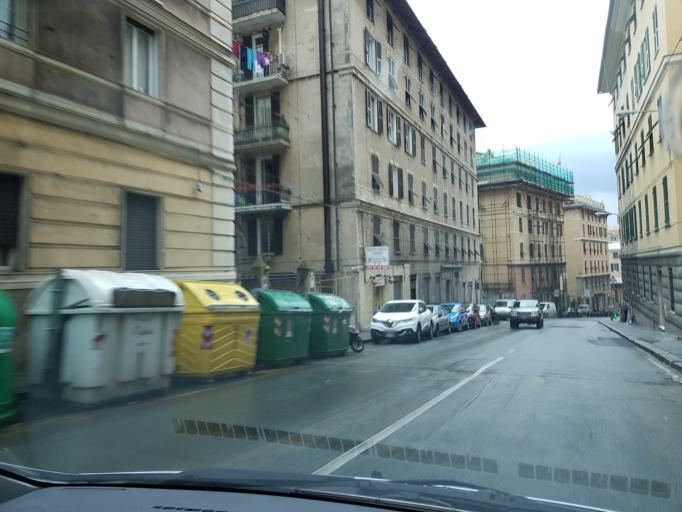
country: IT
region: Liguria
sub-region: Provincia di Genova
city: San Teodoro
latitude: 44.4158
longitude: 8.9100
